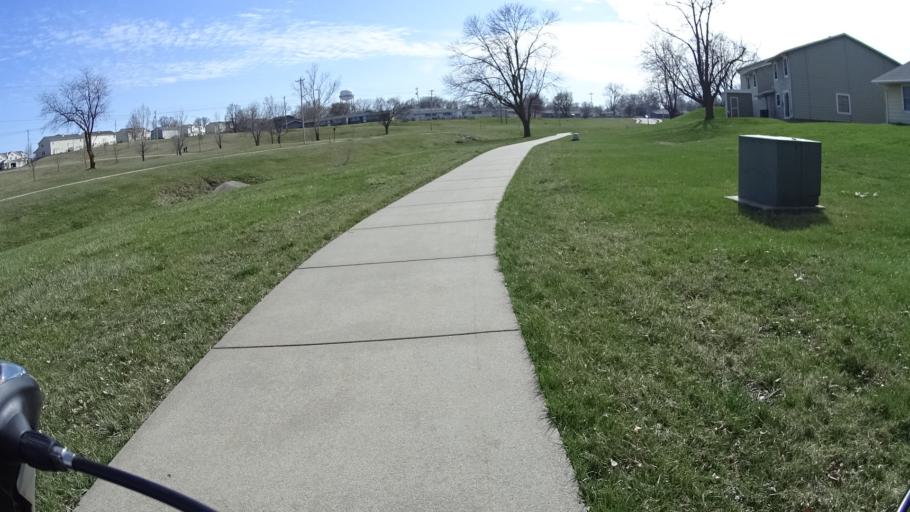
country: US
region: Nebraska
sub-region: Sarpy County
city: Offutt Air Force Base
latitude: 41.1271
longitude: -95.9545
